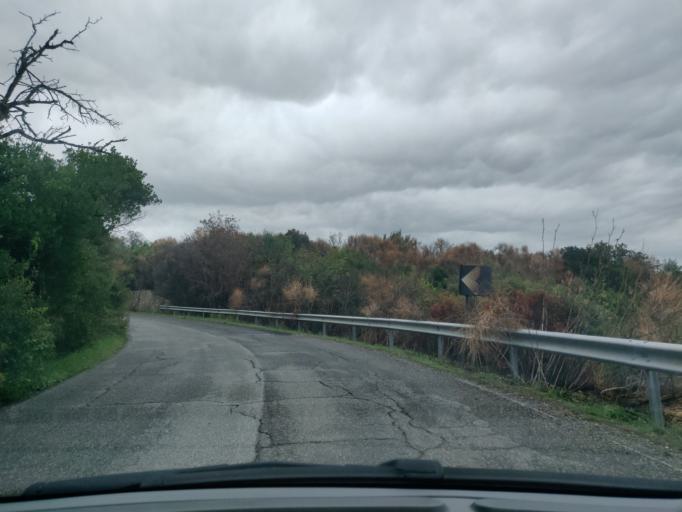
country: IT
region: Latium
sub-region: Citta metropolitana di Roma Capitale
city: Allumiere
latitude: 42.1262
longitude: 11.8555
